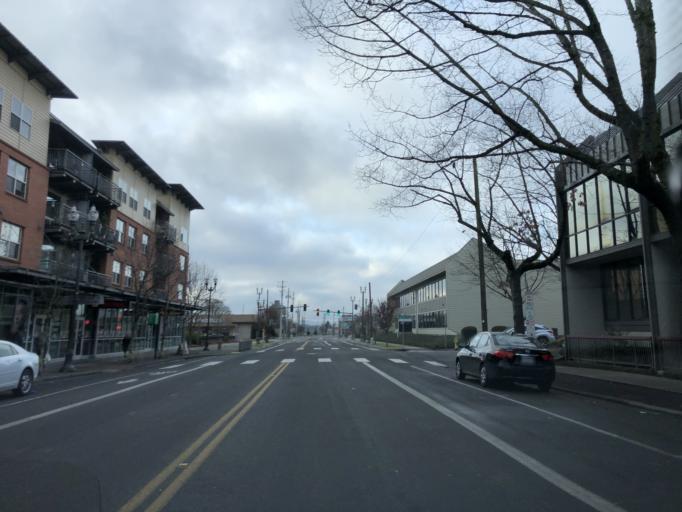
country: US
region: Washington
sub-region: Clark County
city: Vancouver
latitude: 45.6273
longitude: -122.6766
